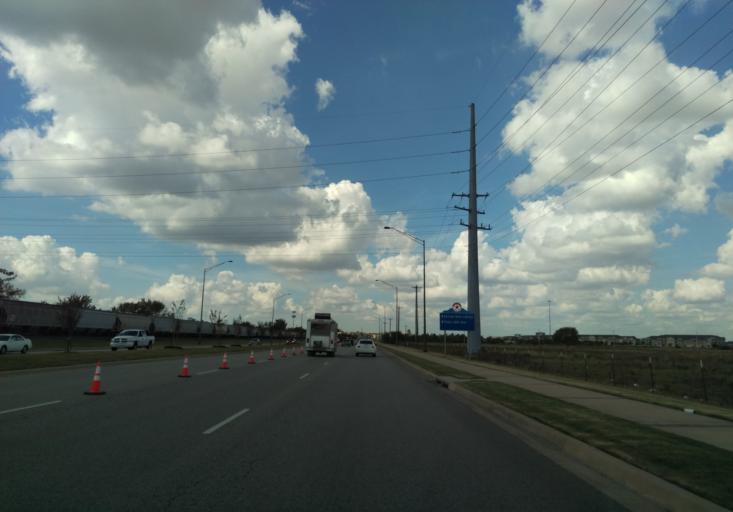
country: US
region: Texas
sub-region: Brazos County
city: College Station
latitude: 30.5815
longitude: -96.3224
